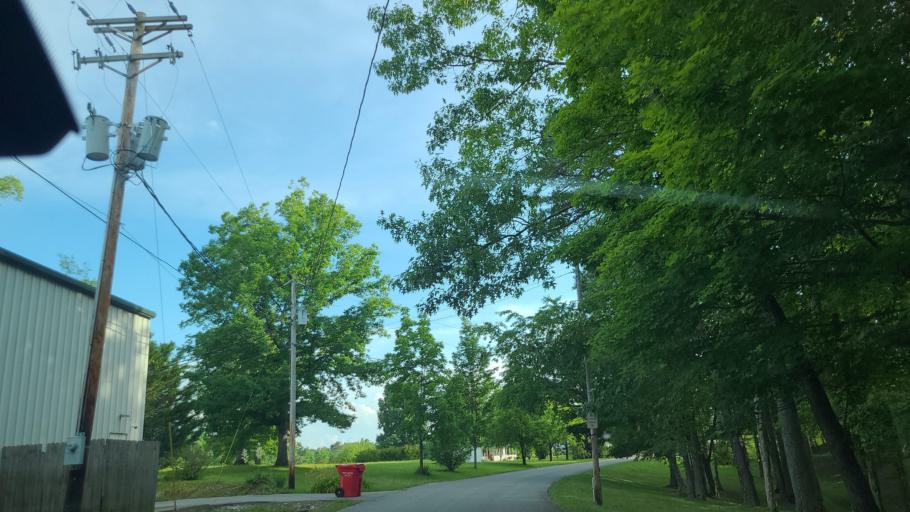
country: US
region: Kentucky
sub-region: Whitley County
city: Corbin
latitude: 36.8944
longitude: -84.2307
